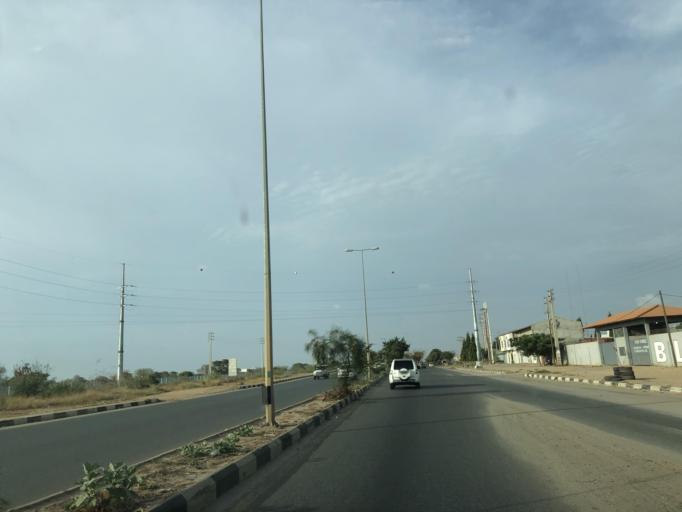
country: AO
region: Luanda
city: Luanda
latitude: -8.9407
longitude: 13.2948
